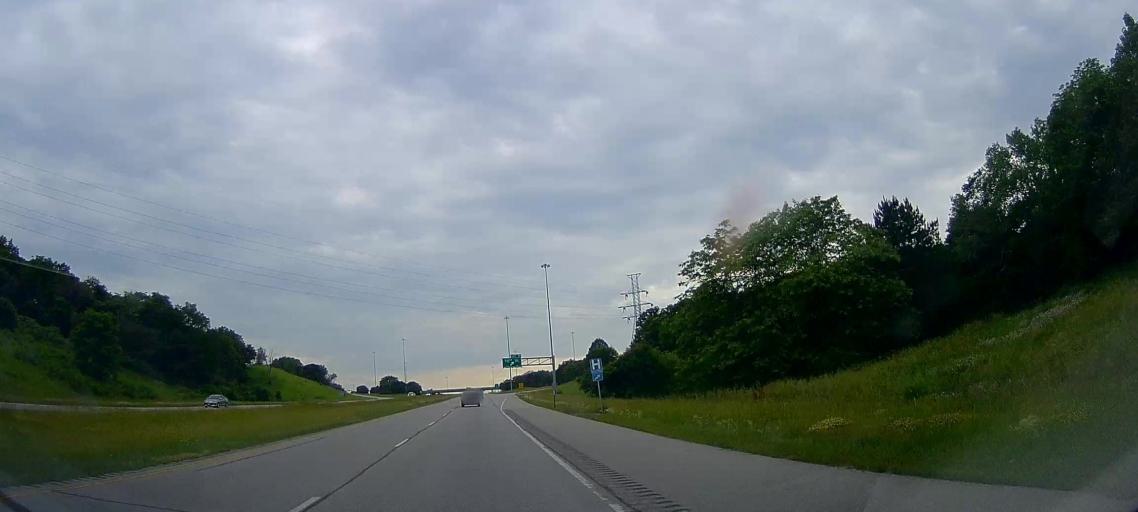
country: US
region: Iowa
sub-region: Pottawattamie County
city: Carter Lake
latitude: 41.3437
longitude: -96.0172
